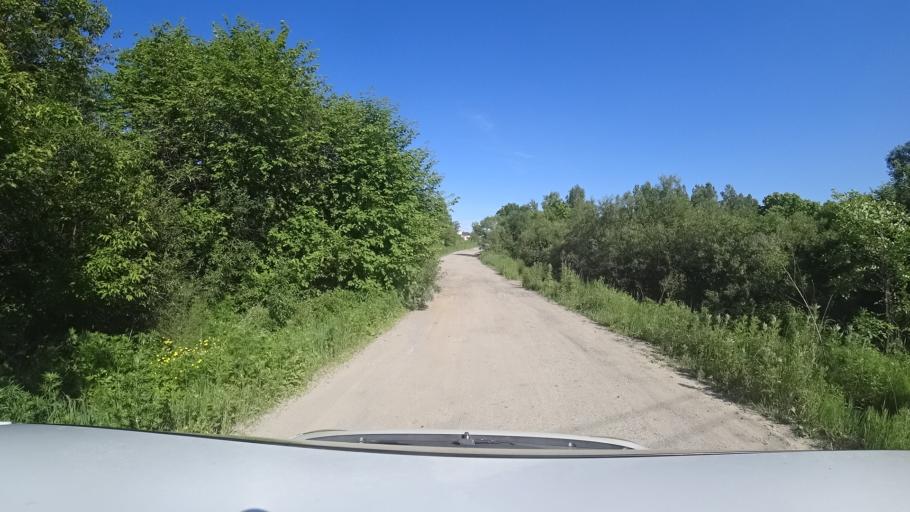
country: RU
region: Khabarovsk Krai
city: Topolevo
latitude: 48.5521
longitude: 135.1872
